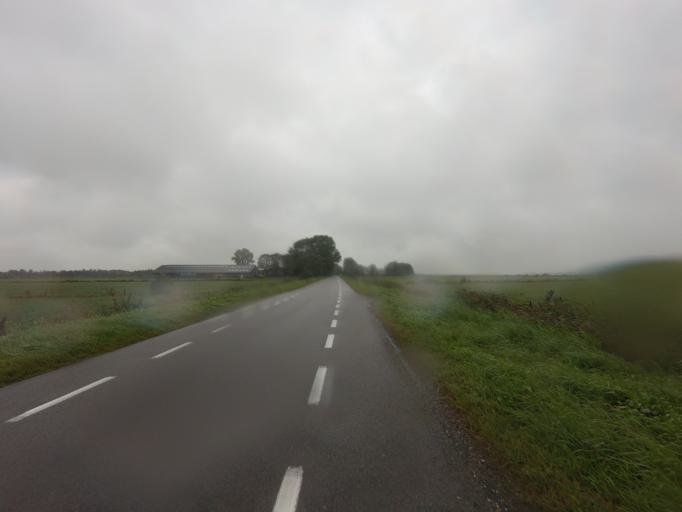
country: NL
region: Friesland
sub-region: Gemeente Smallingerland
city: Oudega
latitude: 53.0964
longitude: 5.9632
